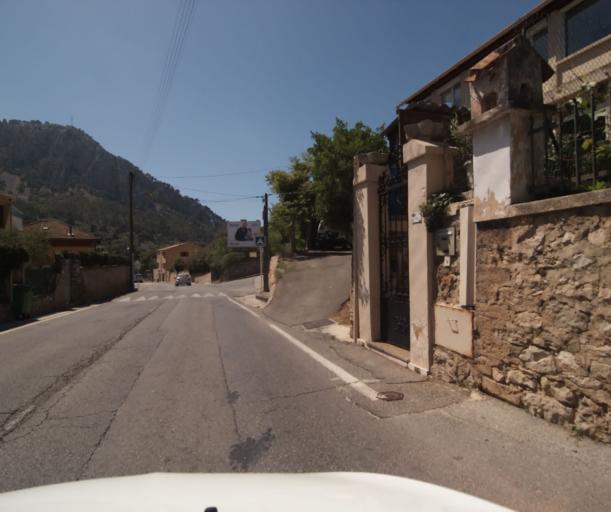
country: FR
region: Provence-Alpes-Cote d'Azur
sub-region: Departement du Var
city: Le Revest-les-Eaux
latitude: 43.1600
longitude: 5.9173
